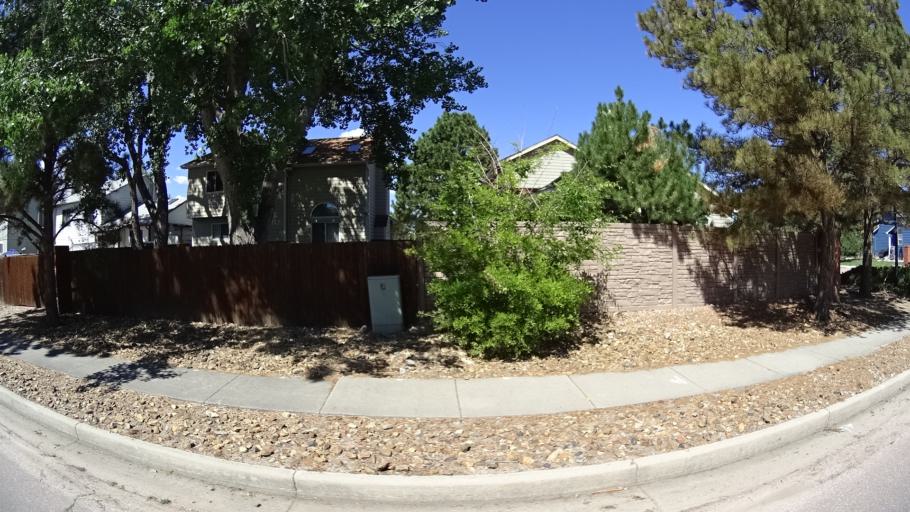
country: US
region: Colorado
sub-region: El Paso County
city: Security-Widefield
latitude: 38.7650
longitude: -104.6551
